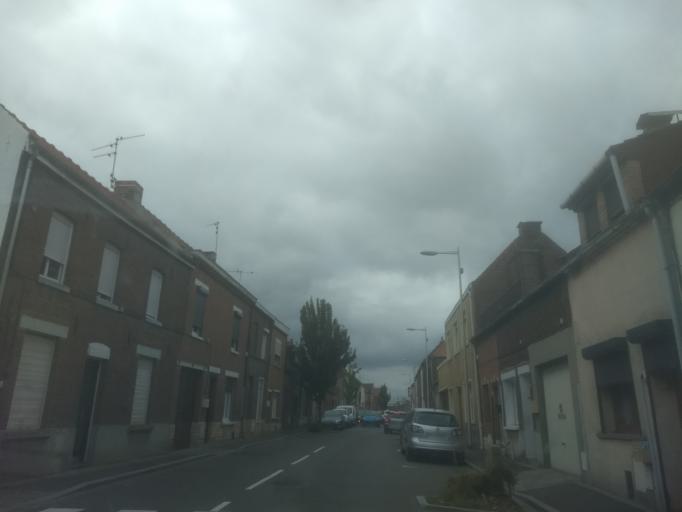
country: FR
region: Nord-Pas-de-Calais
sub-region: Departement du Pas-de-Calais
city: Carvin
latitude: 50.4838
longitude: 2.9617
